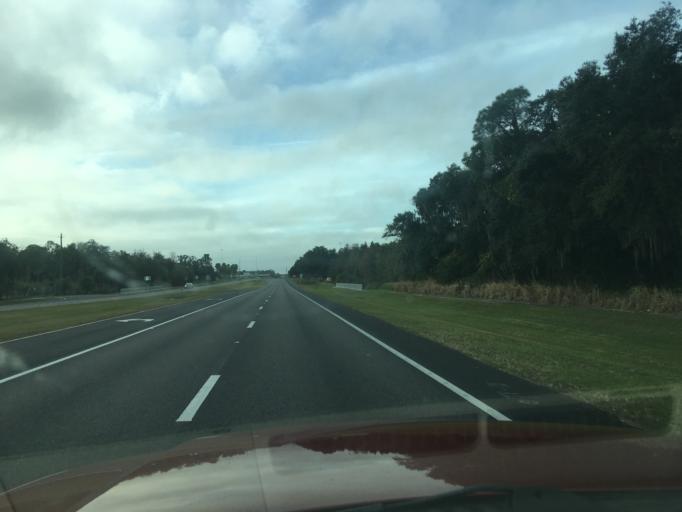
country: US
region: Florida
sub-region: Hillsborough County
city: Plant City
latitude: 28.0446
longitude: -82.1044
